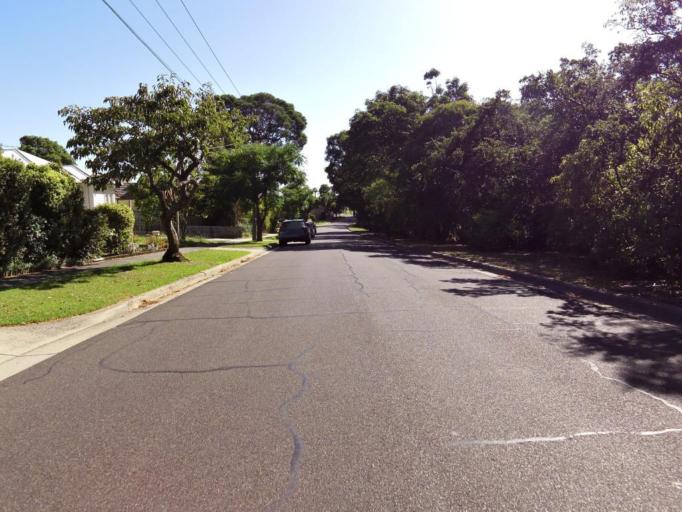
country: AU
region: Victoria
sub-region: Monash
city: Ashwood
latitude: -37.8751
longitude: 145.1161
